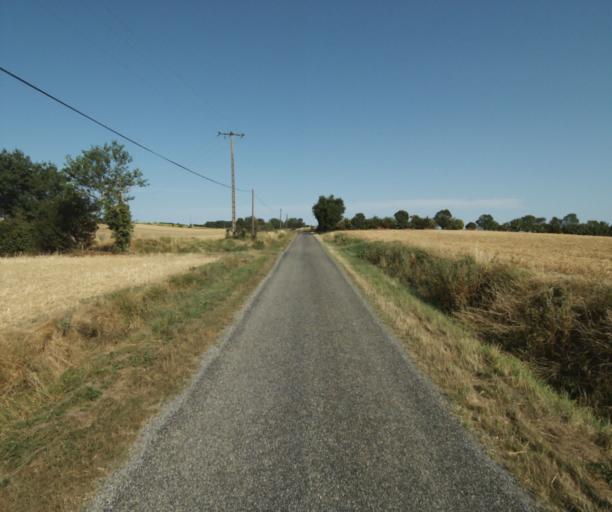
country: FR
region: Midi-Pyrenees
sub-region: Departement de la Haute-Garonne
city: Saint-Felix-Lauragais
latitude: 43.4252
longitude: 1.8347
